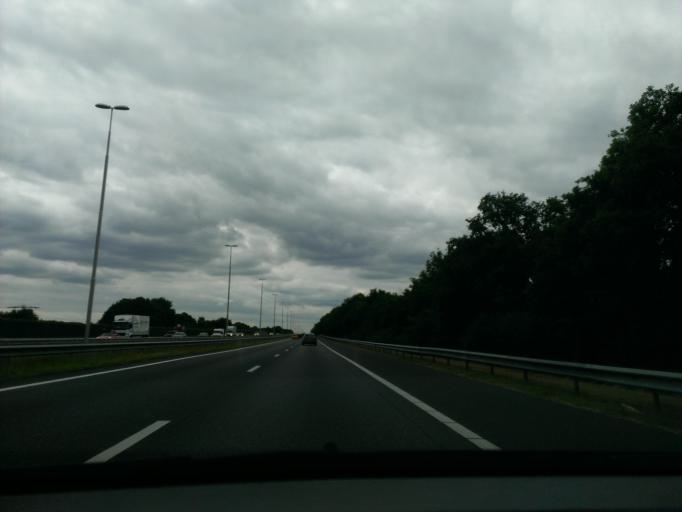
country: NL
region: Gelderland
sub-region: Gemeente Apeldoorn
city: Apeldoorn
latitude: 52.2247
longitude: 6.0192
